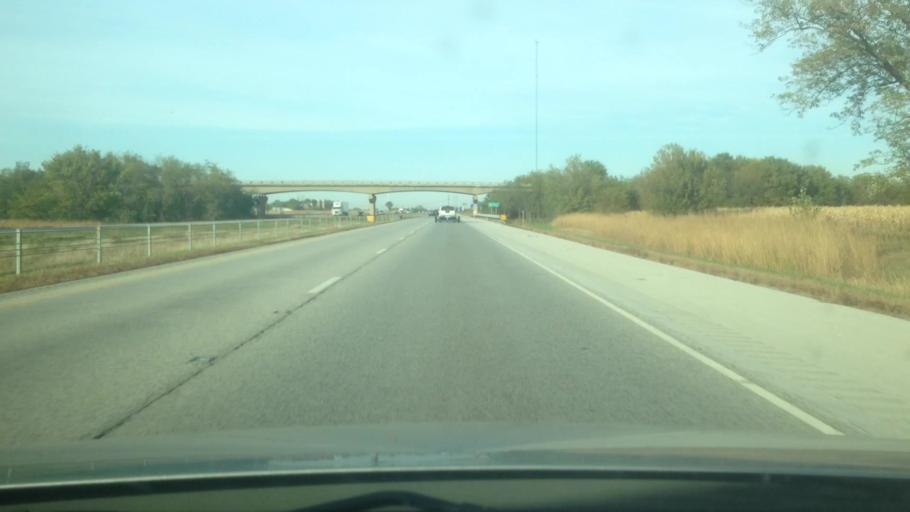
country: US
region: Illinois
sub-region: Kankakee County
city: Manteno
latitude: 41.2935
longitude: -87.8313
